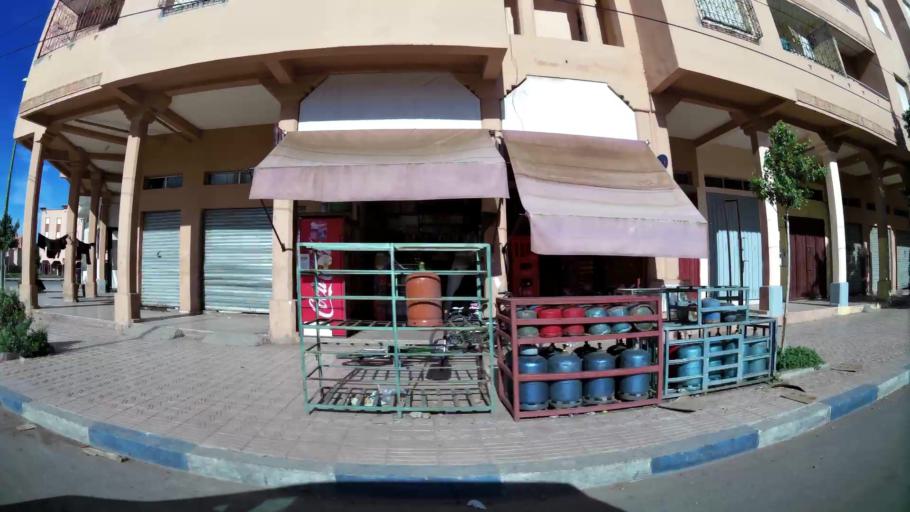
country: MA
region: Marrakech-Tensift-Al Haouz
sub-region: Marrakech
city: Marrakesh
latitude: 31.6888
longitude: -8.0751
